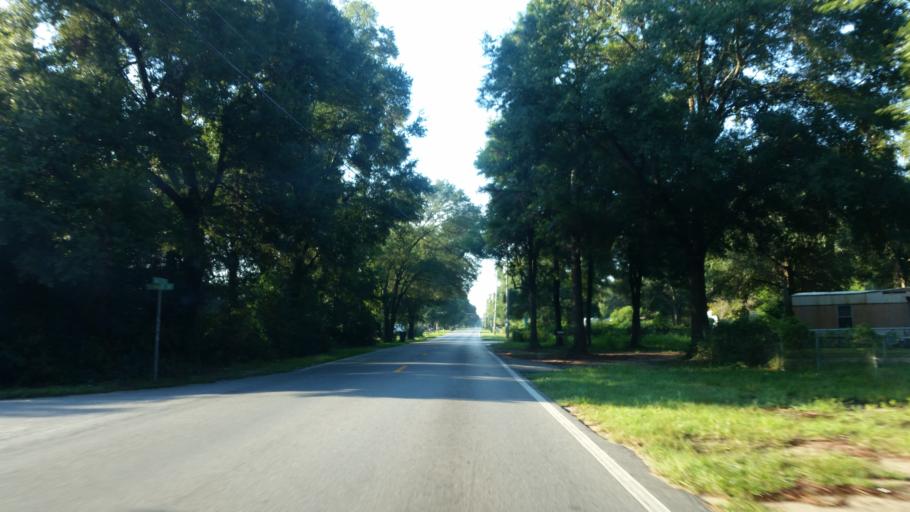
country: US
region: Florida
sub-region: Santa Rosa County
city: Bagdad
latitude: 30.5956
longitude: -87.0650
